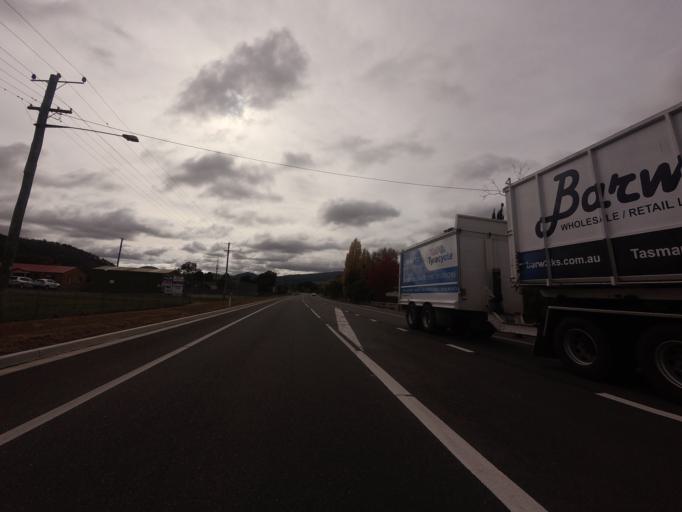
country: AU
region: Tasmania
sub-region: Brighton
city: Bridgewater
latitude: -42.6169
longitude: 147.2222
